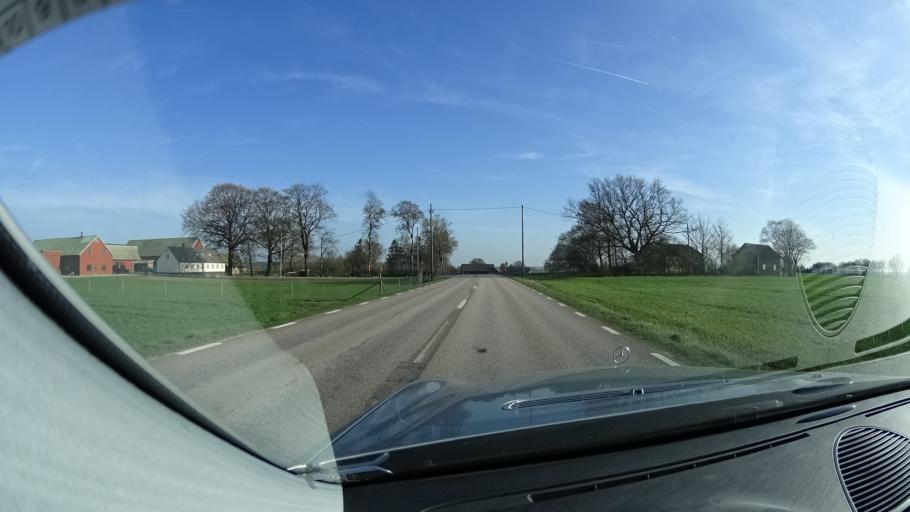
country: SE
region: Skane
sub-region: Landskrona
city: Asmundtorp
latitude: 55.9518
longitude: 12.9467
